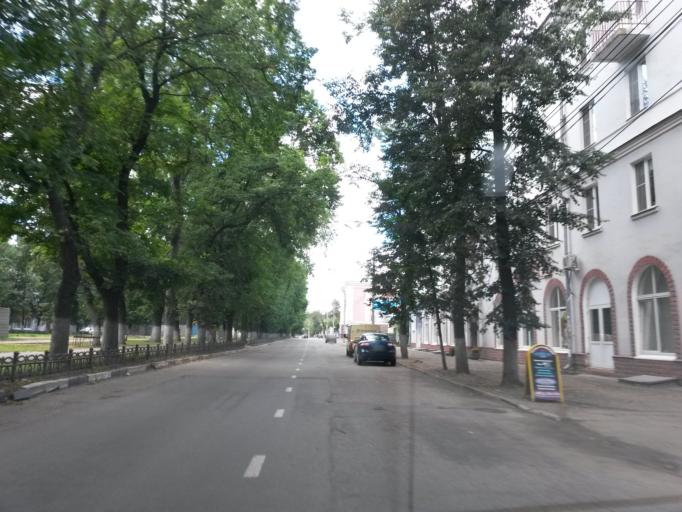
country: RU
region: Jaroslavl
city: Yaroslavl
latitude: 57.6419
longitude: 39.8787
